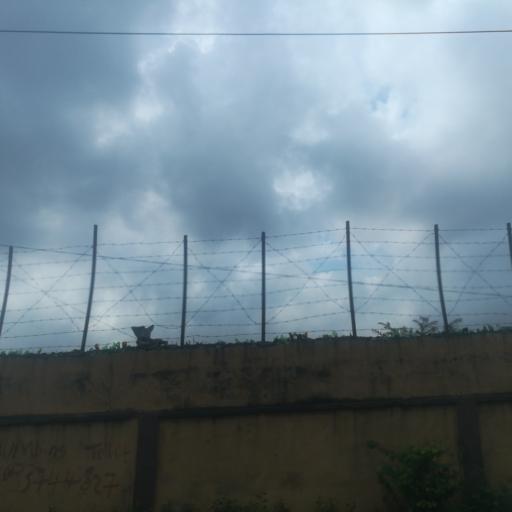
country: NG
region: Lagos
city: Ojota
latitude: 6.6024
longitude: 3.3917
